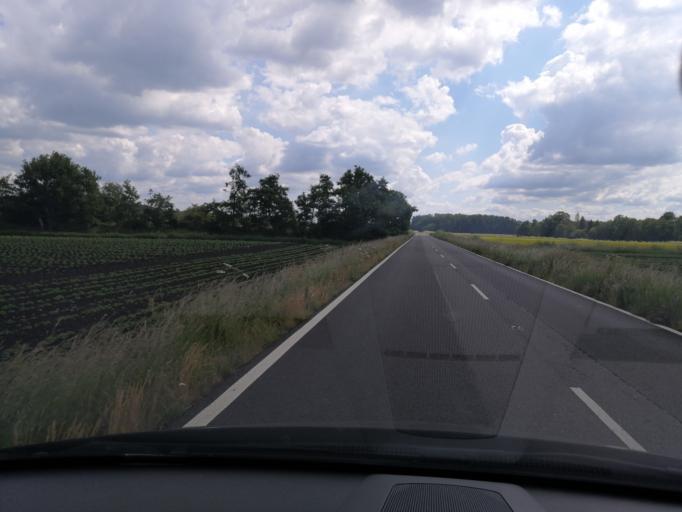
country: GB
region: England
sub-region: Cambridgeshire
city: Yaxley
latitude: 52.4894
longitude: -0.2433
